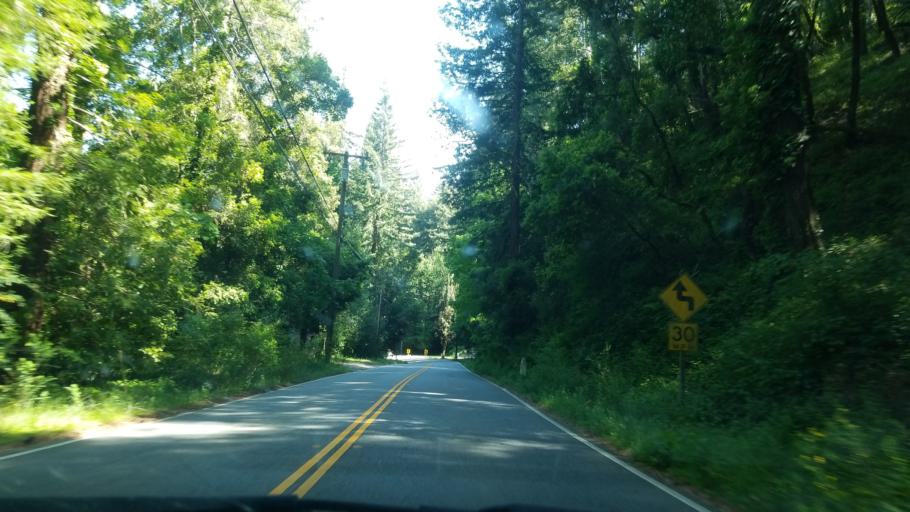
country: US
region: California
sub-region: Santa Cruz County
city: Scotts Valley
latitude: 37.0842
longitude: -121.9503
